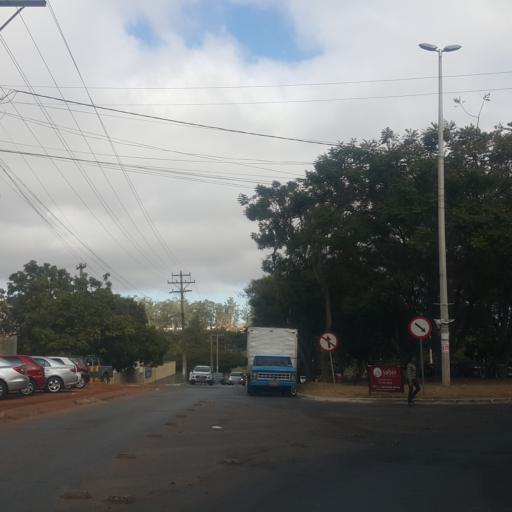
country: BR
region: Federal District
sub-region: Brasilia
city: Brasilia
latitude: -15.8237
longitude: -48.0676
